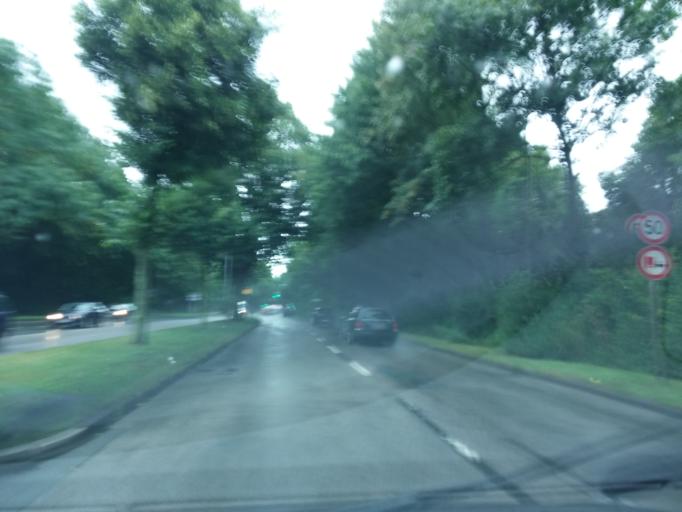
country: DE
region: North Rhine-Westphalia
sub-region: Regierungsbezirk Munster
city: Gelsenkirchen
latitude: 51.5599
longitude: 7.0738
